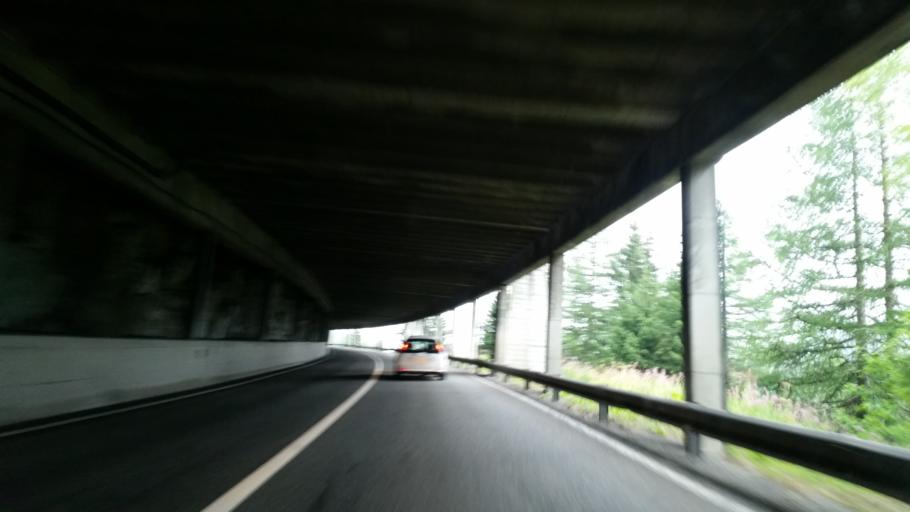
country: CH
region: Valais
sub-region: Entremont District
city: Orsieres
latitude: 45.9451
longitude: 7.2091
